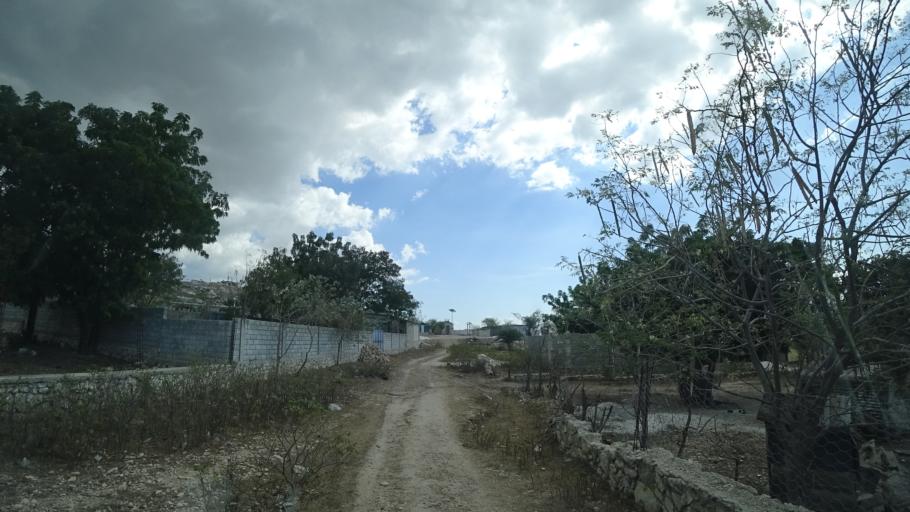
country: HT
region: Ouest
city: Cabaret
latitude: 18.6777
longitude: -72.3168
